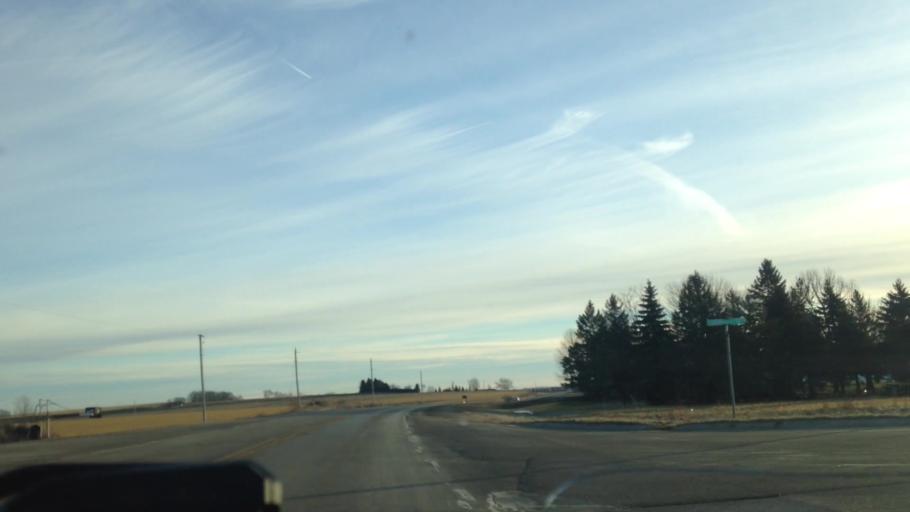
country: US
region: Wisconsin
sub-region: Dodge County
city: Mayville
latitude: 43.5151
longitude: -88.5265
